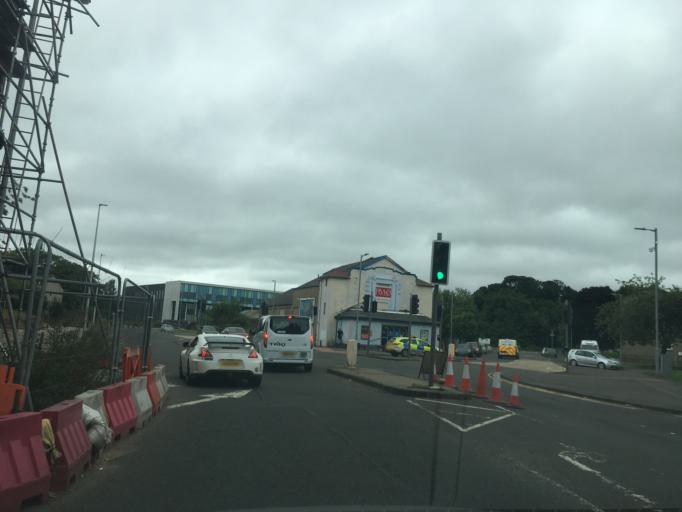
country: GB
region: Scotland
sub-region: Renfrewshire
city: Renfrew
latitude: 55.8798
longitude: -4.3855
